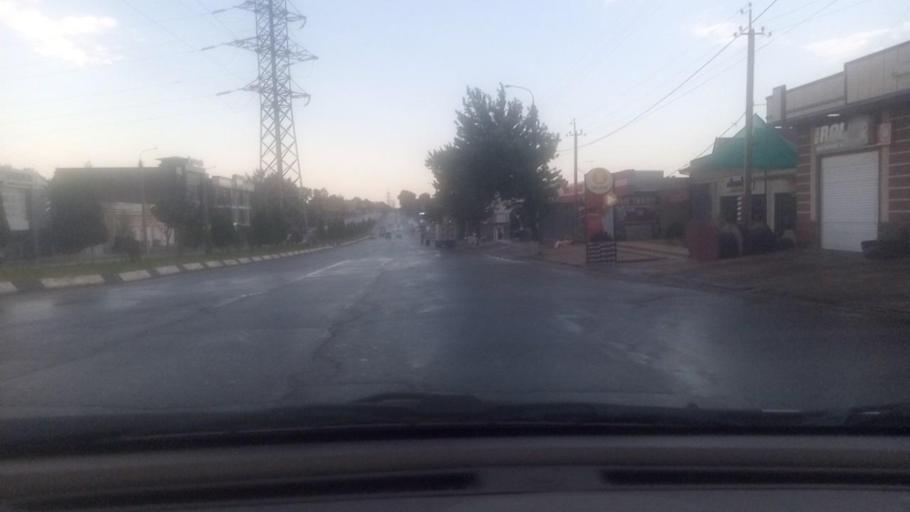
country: UZ
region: Toshkent Shahri
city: Tashkent
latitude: 41.3067
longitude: 69.1935
